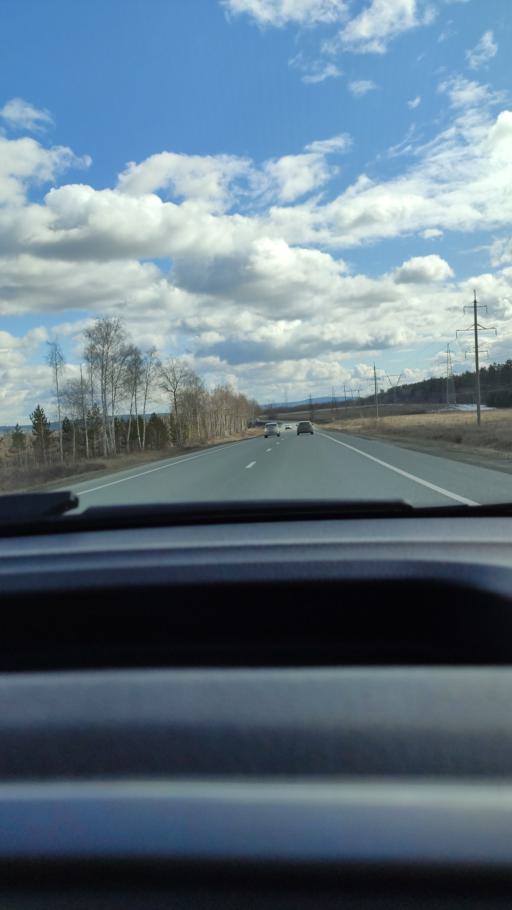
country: RU
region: Samara
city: Bogatyr'
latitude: 53.4950
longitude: 49.9648
